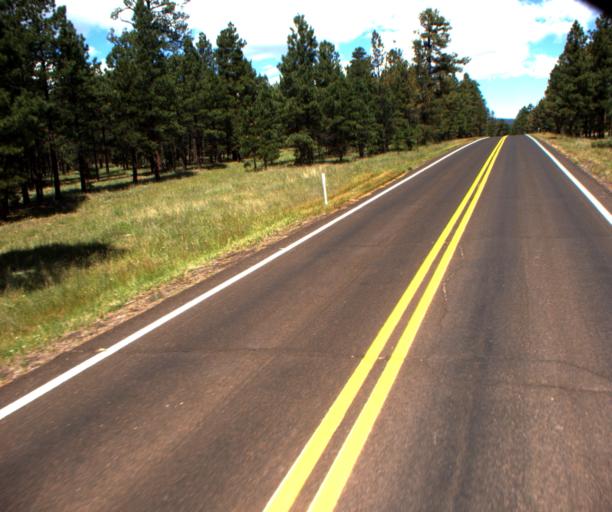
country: US
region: Arizona
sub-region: Apache County
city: Eagar
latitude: 34.0360
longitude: -109.4533
